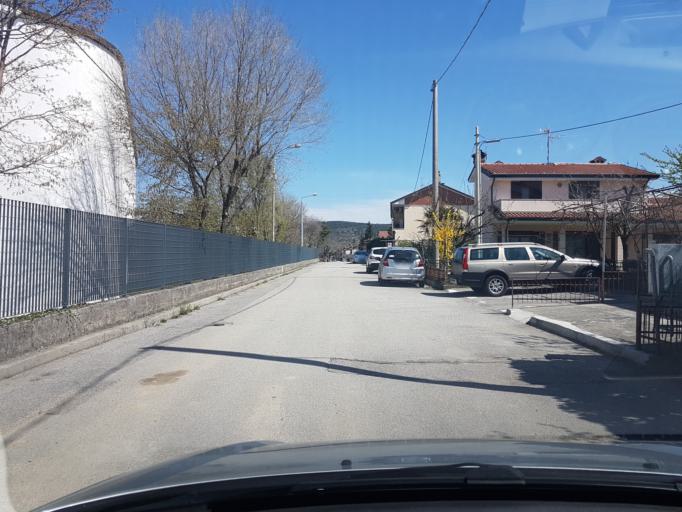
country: IT
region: Friuli Venezia Giulia
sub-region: Provincia di Trieste
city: Sistiana-Visogliano
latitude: 45.7639
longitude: 13.6414
